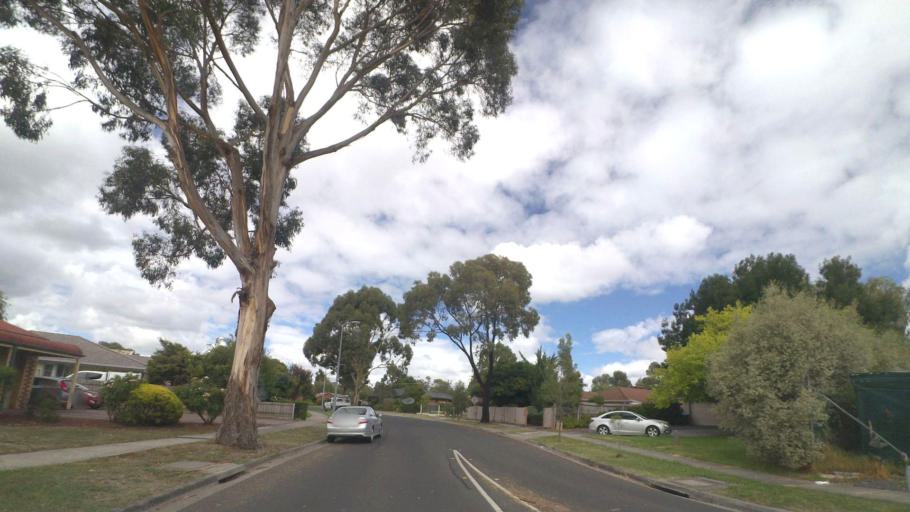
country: AU
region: Victoria
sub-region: Maroondah
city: Bayswater North
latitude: -37.8318
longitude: 145.3036
